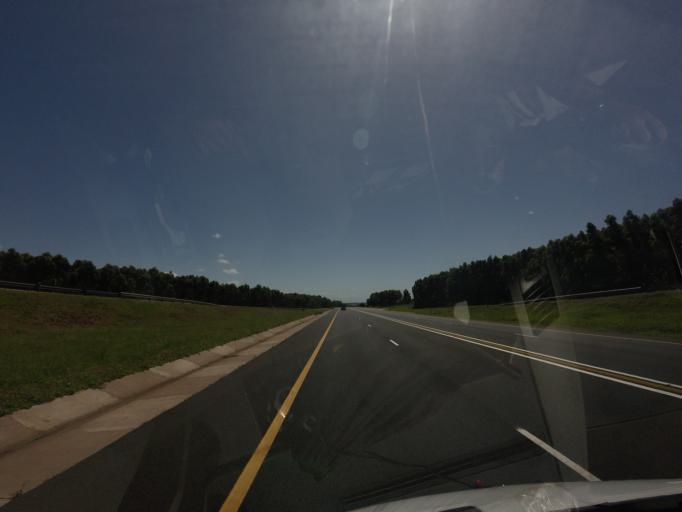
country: ZA
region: KwaZulu-Natal
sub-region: uThungulu District Municipality
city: eSikhawini
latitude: -28.9939
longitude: 31.6985
